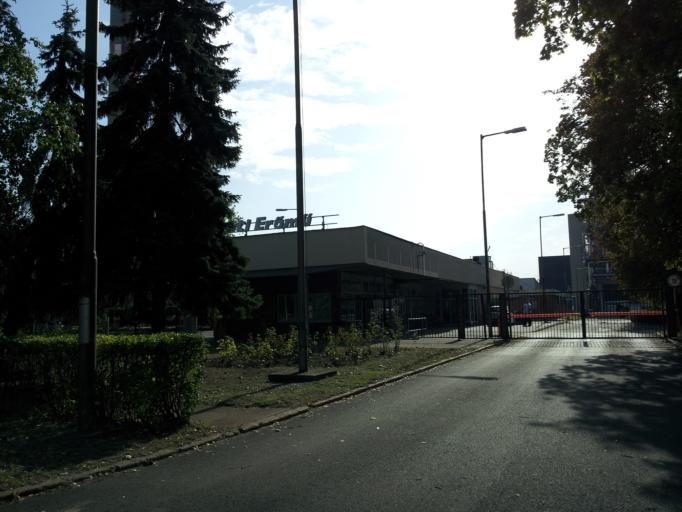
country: HU
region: Pest
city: Szazhalombatta
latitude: 47.3284
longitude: 18.9207
